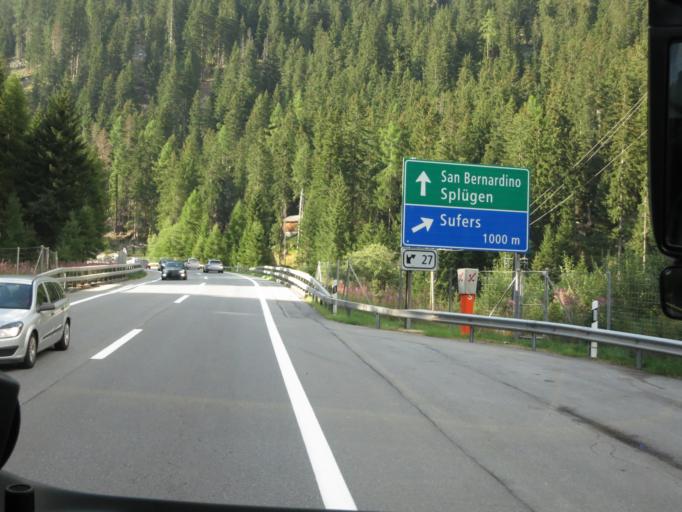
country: CH
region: Grisons
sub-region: Hinterrhein District
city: Thusis
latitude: 46.5691
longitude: 9.3821
